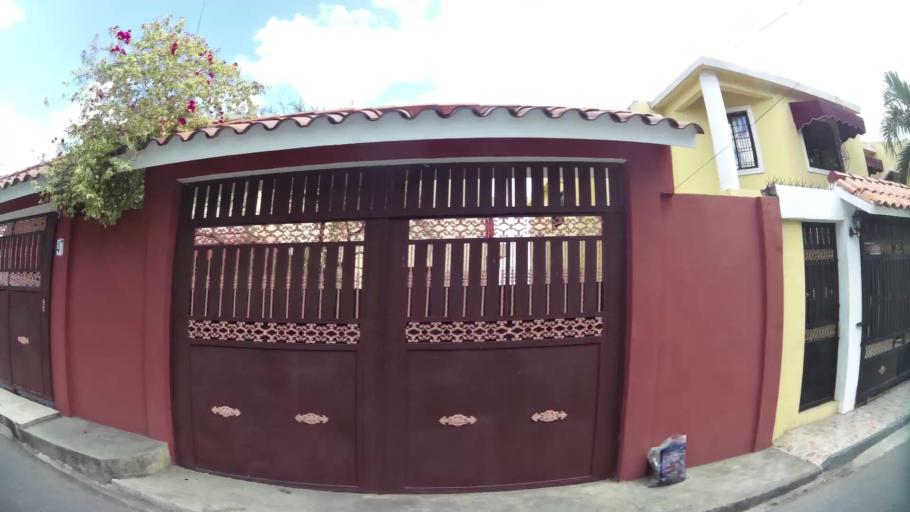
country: DO
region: Nacional
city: Ensanche Luperon
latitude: 18.5237
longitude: -69.9082
